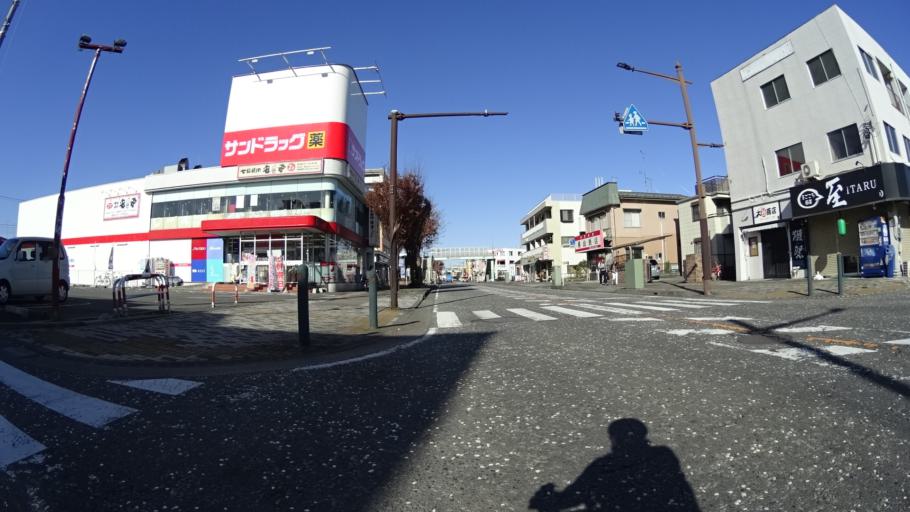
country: JP
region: Kanagawa
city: Zama
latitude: 35.5655
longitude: 139.3608
